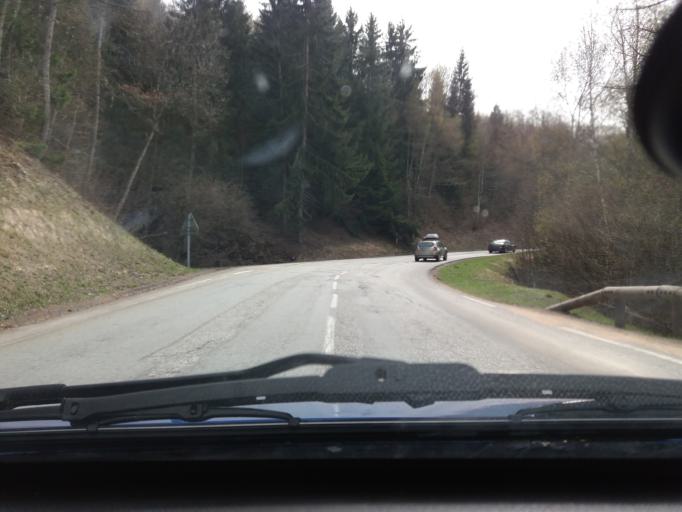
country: FR
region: Rhone-Alpes
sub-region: Departement de la Savoie
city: Macot-la-Plagne
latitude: 45.5482
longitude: 6.6703
